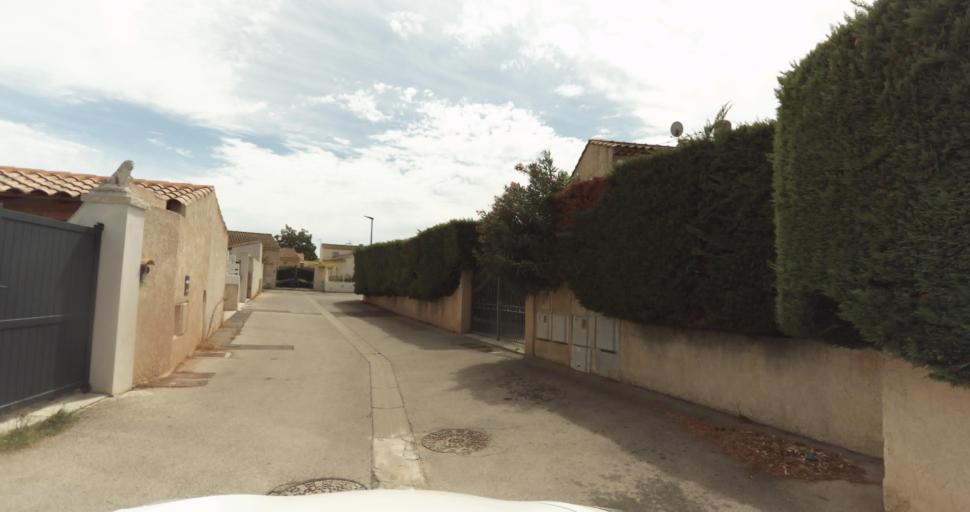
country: FR
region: Provence-Alpes-Cote d'Azur
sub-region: Departement des Bouches-du-Rhone
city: Miramas
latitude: 43.5846
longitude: 5.0157
